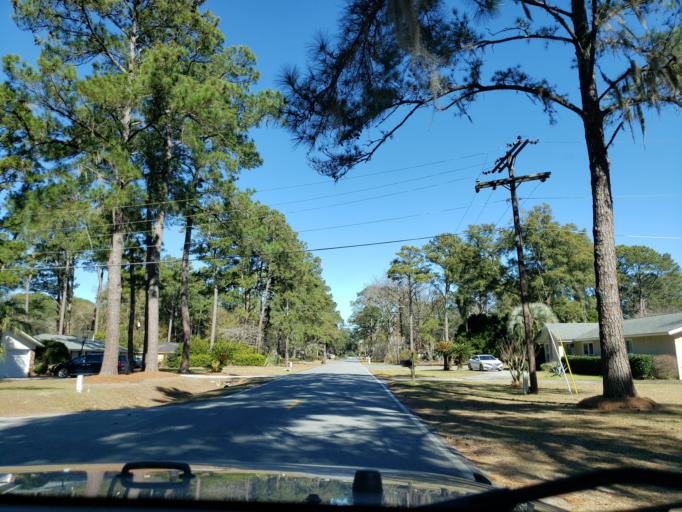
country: US
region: Georgia
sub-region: Chatham County
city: Wilmington Island
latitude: 32.0340
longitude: -80.9725
